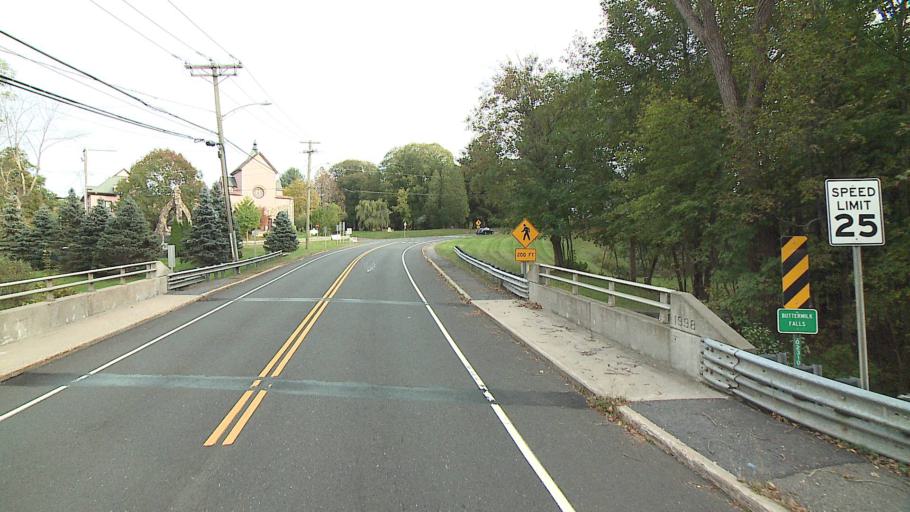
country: US
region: Connecticut
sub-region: Litchfield County
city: Winchester Center
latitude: 41.9944
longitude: -73.2028
